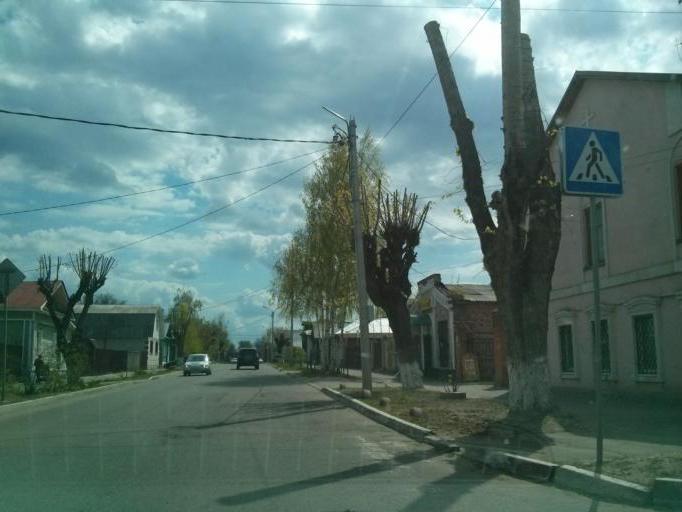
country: RU
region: Vladimir
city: Murom
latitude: 55.5701
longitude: 42.0638
